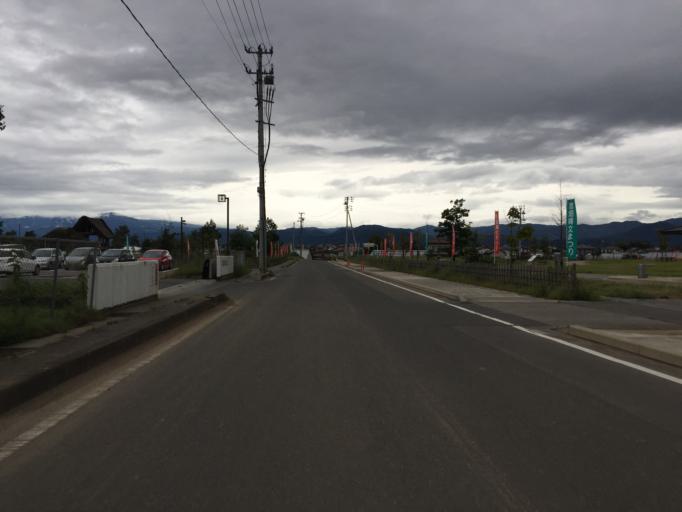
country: JP
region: Fukushima
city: Hobaramachi
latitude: 37.7909
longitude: 140.5172
